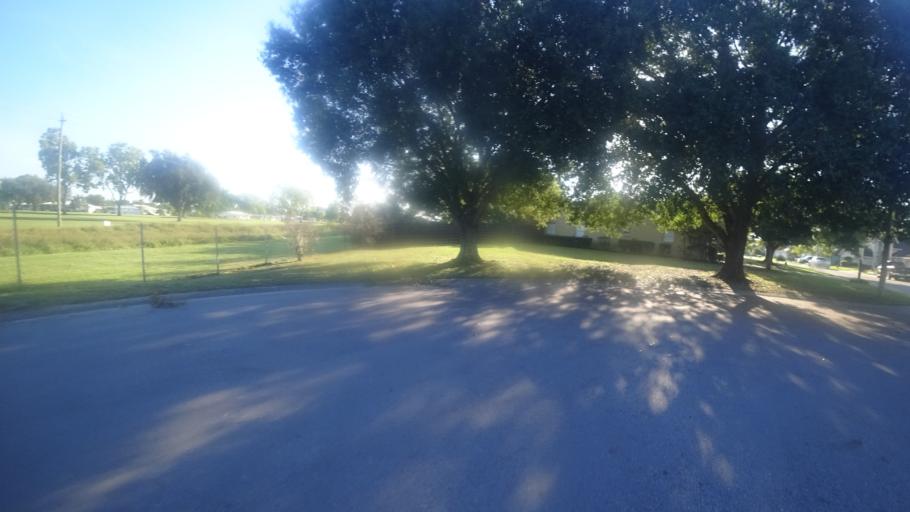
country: US
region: Florida
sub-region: Manatee County
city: Ellenton
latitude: 27.4908
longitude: -82.5090
